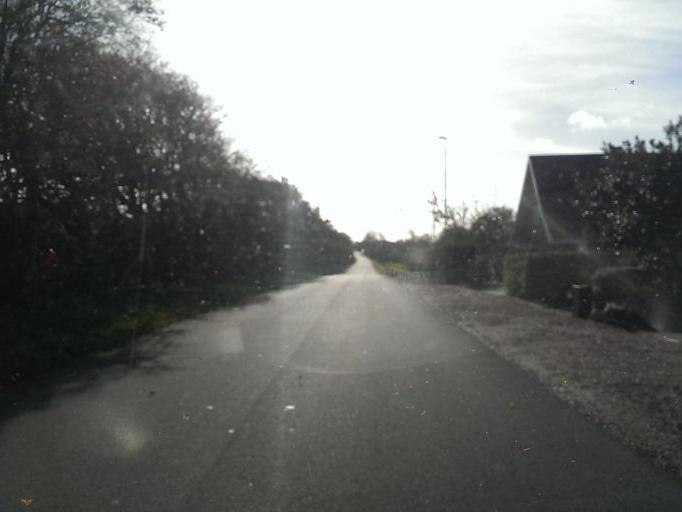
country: DK
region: South Denmark
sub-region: Esbjerg Kommune
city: Tjaereborg
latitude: 55.4636
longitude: 8.5757
